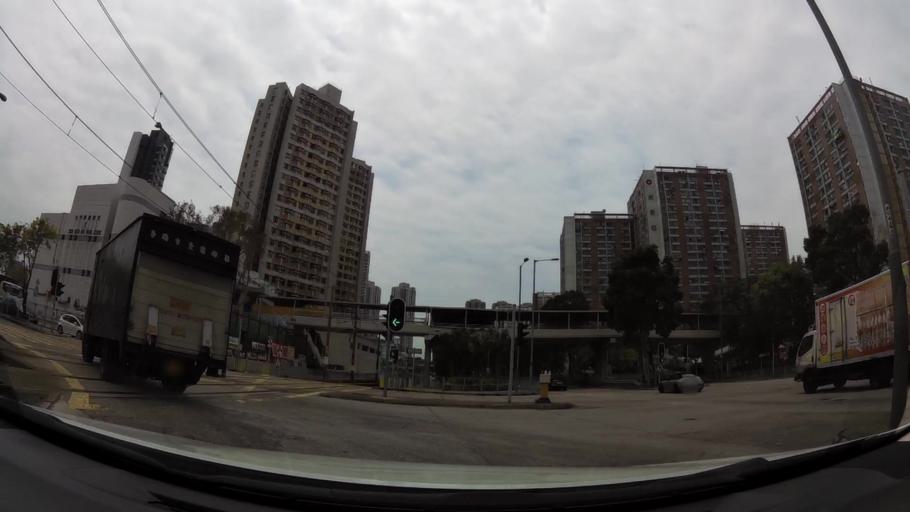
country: HK
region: Tuen Mun
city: Tuen Mun
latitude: 22.3777
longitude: 113.9669
